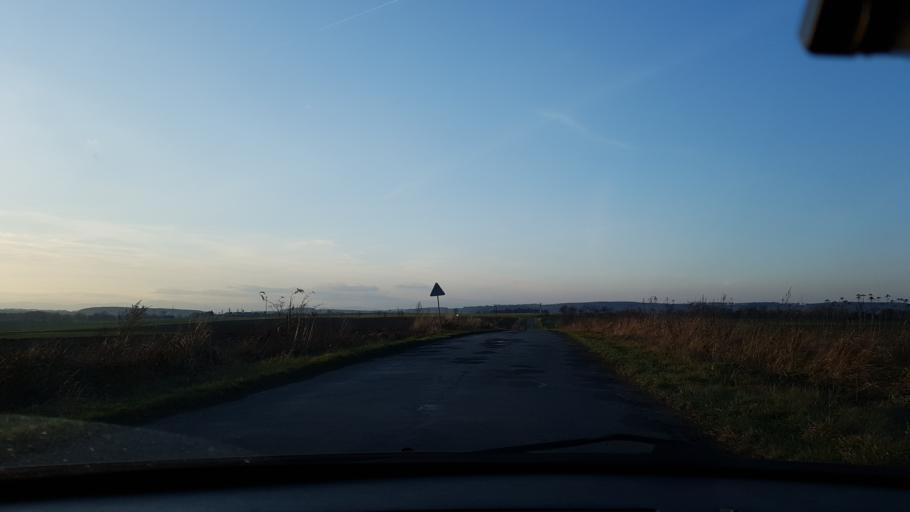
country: PL
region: Lower Silesian Voivodeship
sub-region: Powiat zabkowicki
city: Cieplowody
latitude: 50.6721
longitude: 16.9452
